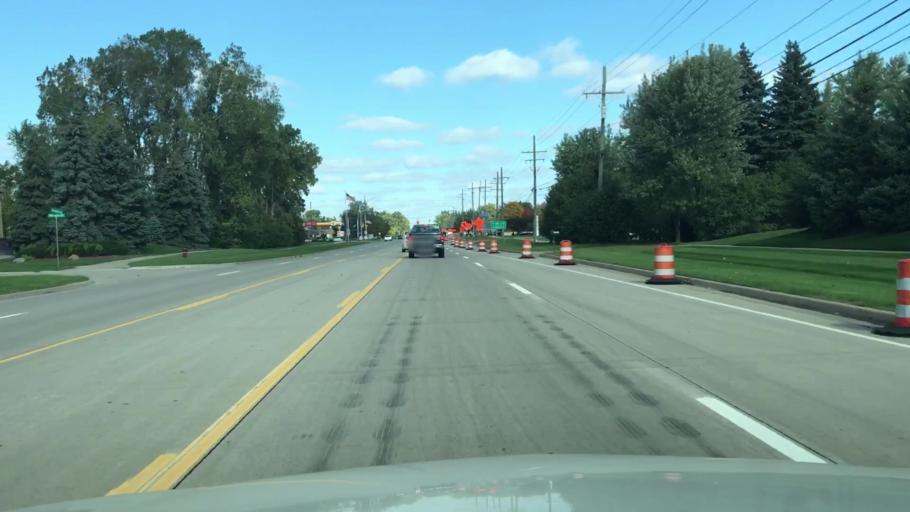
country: US
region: Michigan
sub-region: Macomb County
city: Sterling Heights
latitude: 42.5904
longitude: -83.0897
